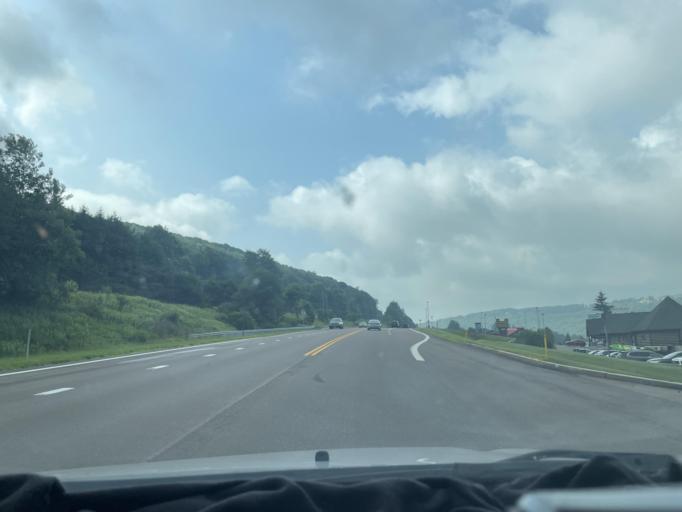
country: US
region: Maryland
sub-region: Garrett County
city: Oakland
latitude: 39.5519
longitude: -79.3500
